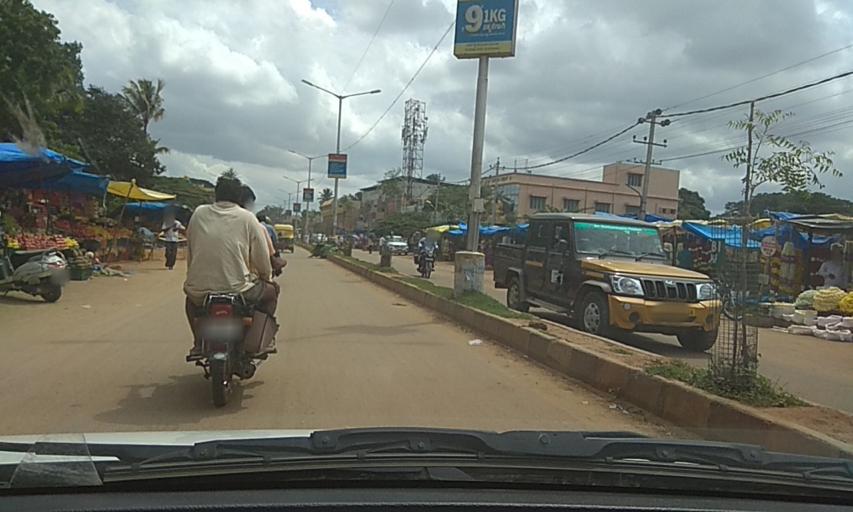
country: IN
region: Karnataka
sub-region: Tumkur
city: Tumkur
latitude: 13.3434
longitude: 77.0988
